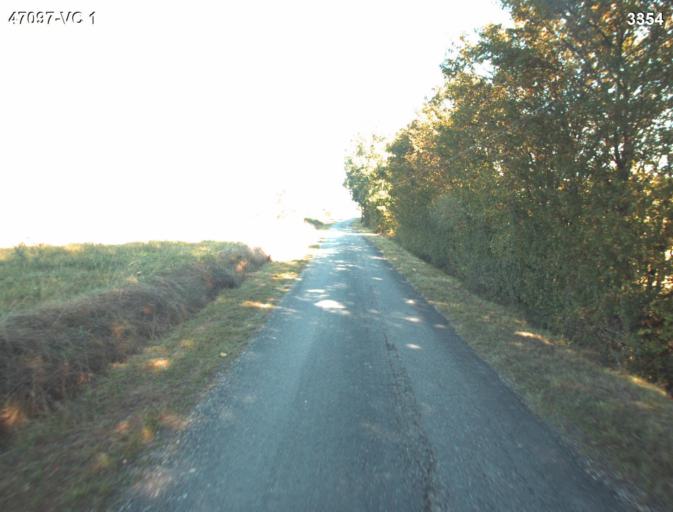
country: FR
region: Aquitaine
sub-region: Departement du Lot-et-Garonne
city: Vianne
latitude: 44.1972
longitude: 0.3630
